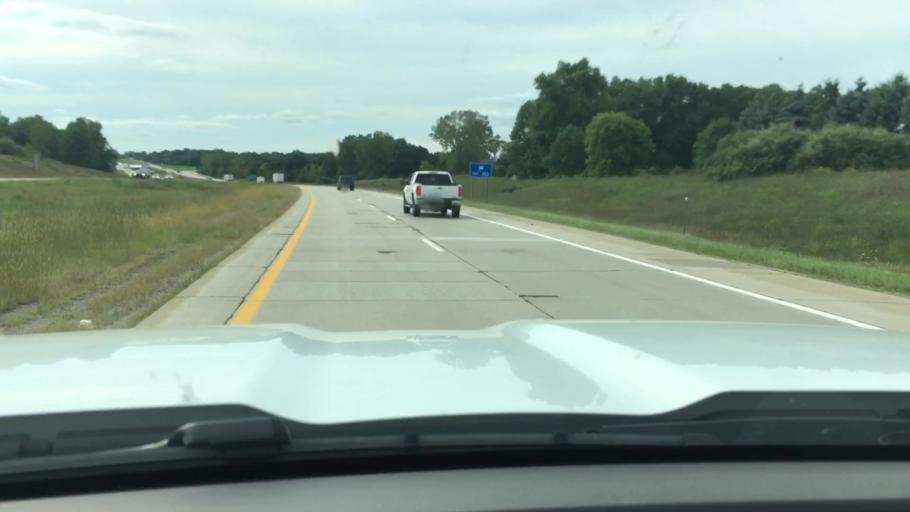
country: US
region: Michigan
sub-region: Lapeer County
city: Lapeer
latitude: 43.0237
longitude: -83.3039
